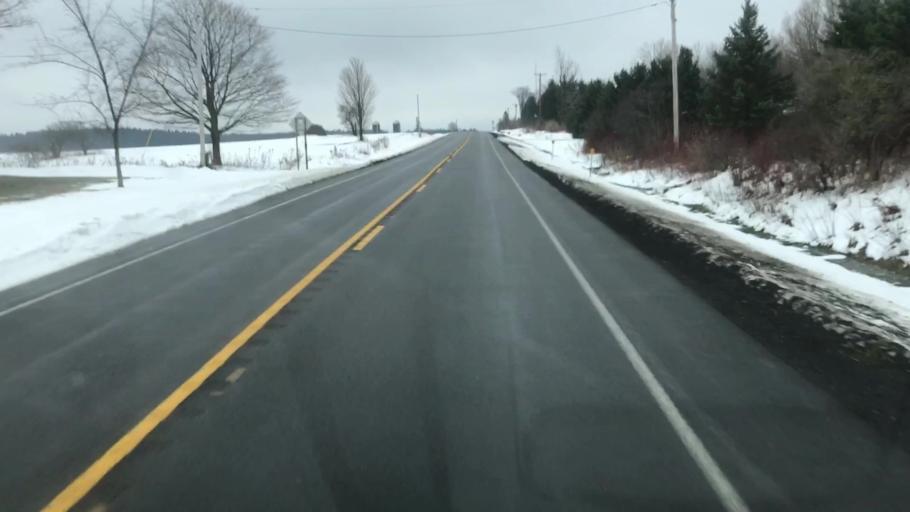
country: US
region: New York
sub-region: Cayuga County
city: Moravia
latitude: 42.7671
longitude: -76.3319
